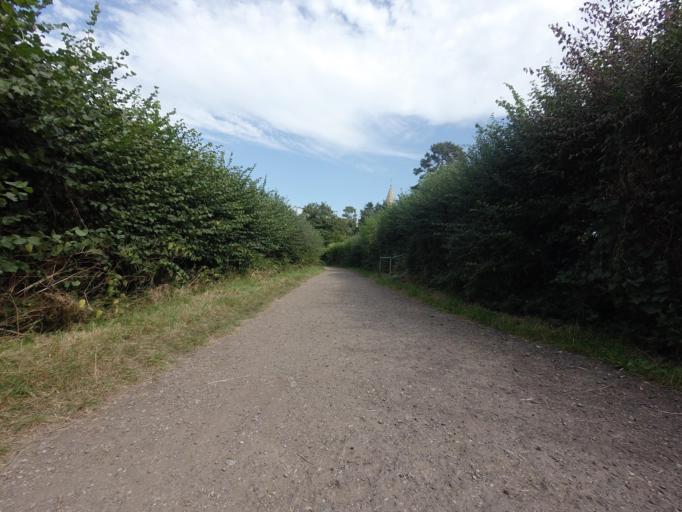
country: GB
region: England
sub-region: Wiltshire
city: Trowbridge
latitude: 51.3317
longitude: -2.1876
